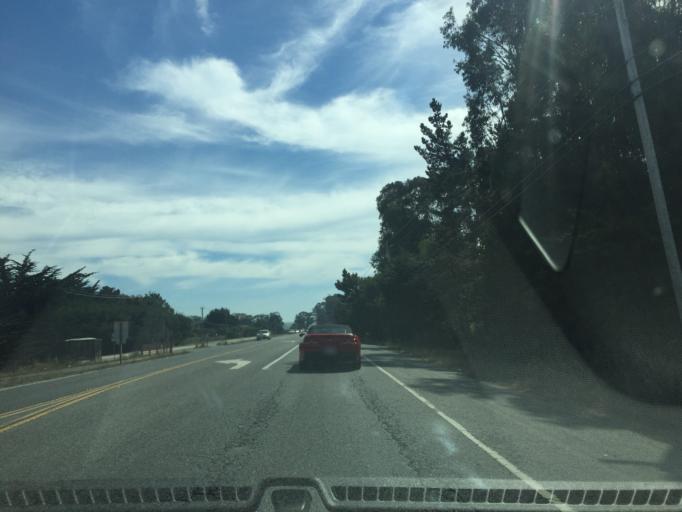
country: US
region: California
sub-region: San Mateo County
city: El Granada
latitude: 37.4888
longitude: -122.4501
